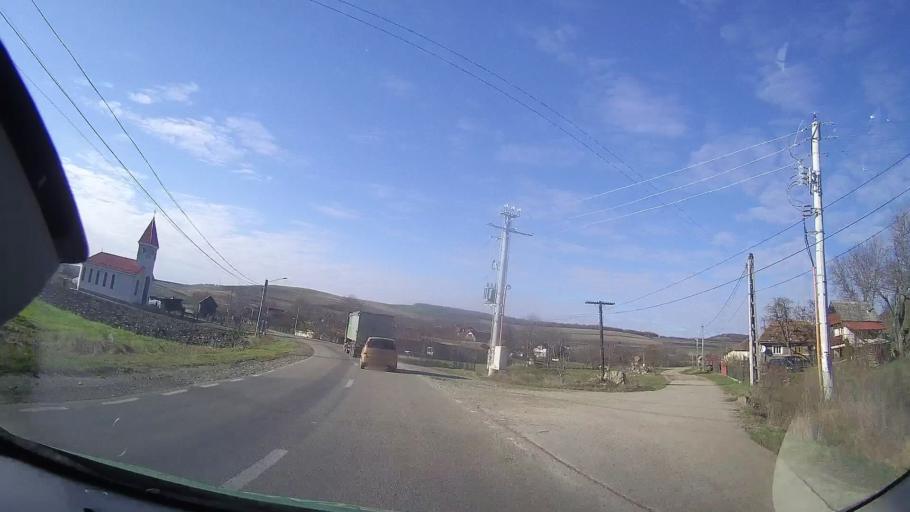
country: RO
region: Cluj
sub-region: Comuna Caianu
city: Vaida-Camaras
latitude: 46.8071
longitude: 23.9724
